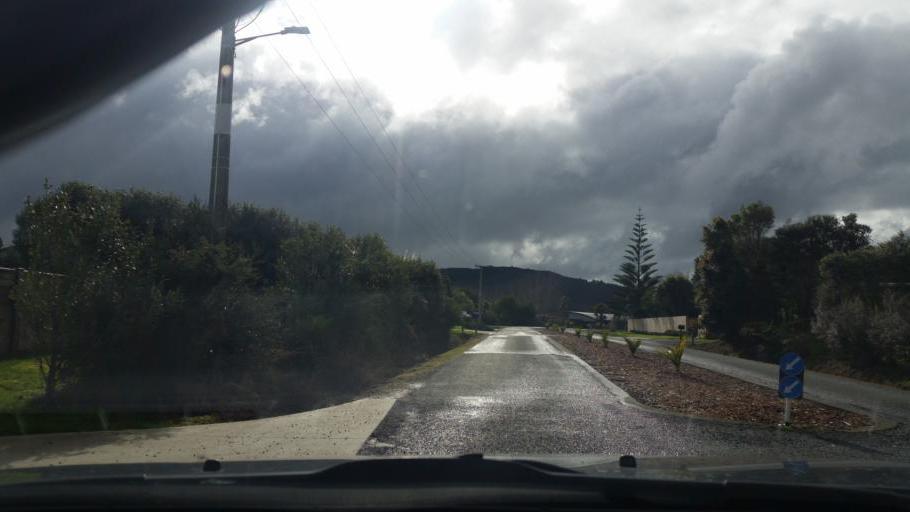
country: NZ
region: Auckland
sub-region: Auckland
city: Wellsford
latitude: -36.0919
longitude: 174.5734
